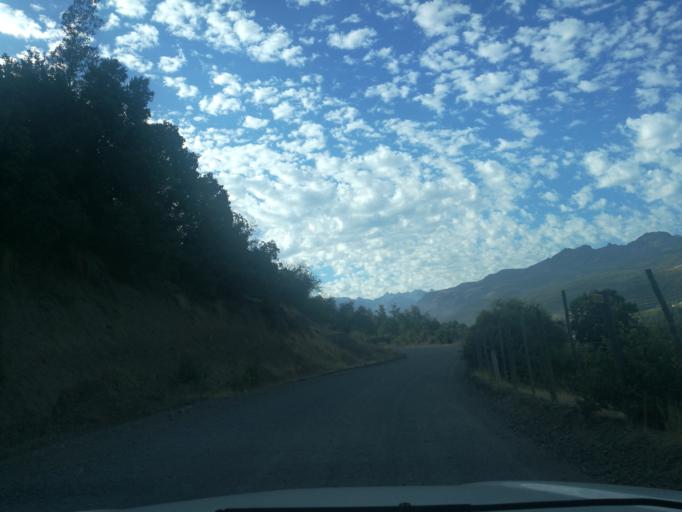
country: CL
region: O'Higgins
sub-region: Provincia de Cachapoal
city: Machali
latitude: -34.2426
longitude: -70.4709
